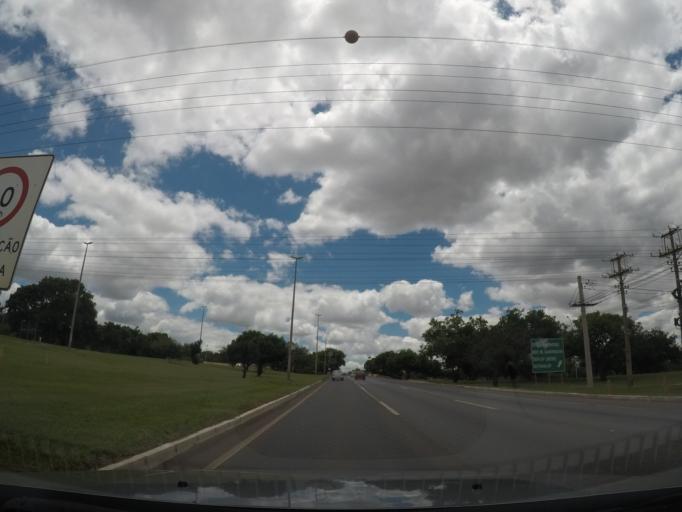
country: BR
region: Federal District
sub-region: Brasilia
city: Brasilia
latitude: -15.7562
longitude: -47.9271
